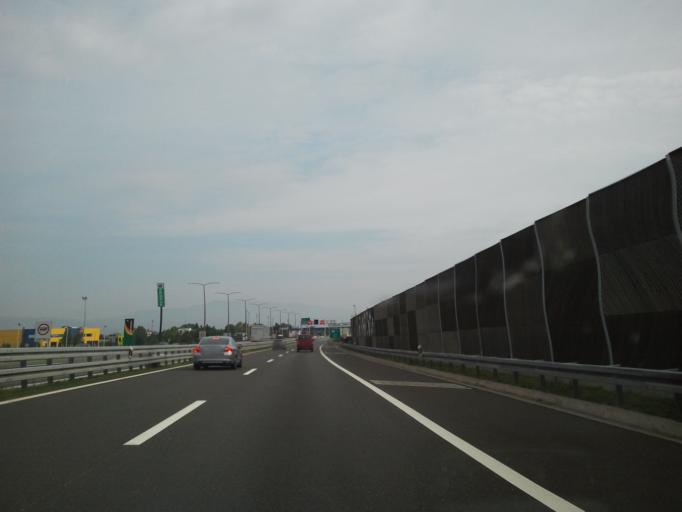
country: HR
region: Grad Zagreb
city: Brezovica
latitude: 45.7444
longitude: 15.8813
